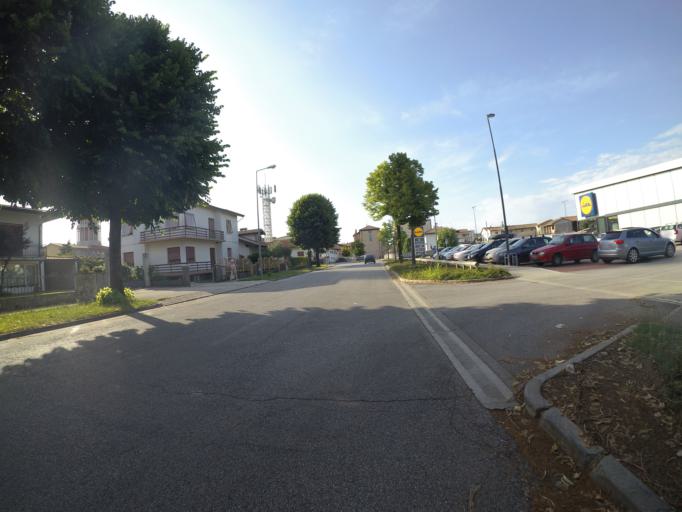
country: IT
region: Friuli Venezia Giulia
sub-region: Provincia di Udine
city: Mortegliano
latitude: 45.9433
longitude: 13.1735
